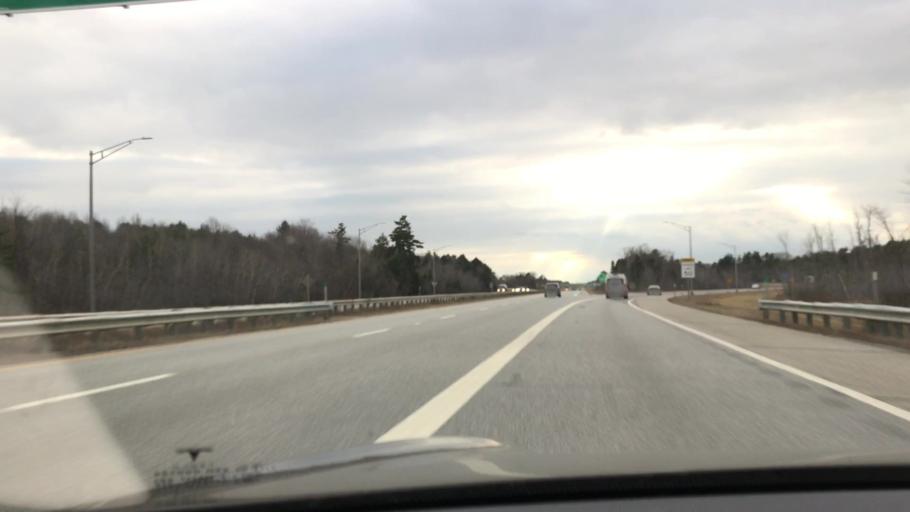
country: US
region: Maine
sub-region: Kennebec County
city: Gardiner
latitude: 44.2250
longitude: -69.8174
